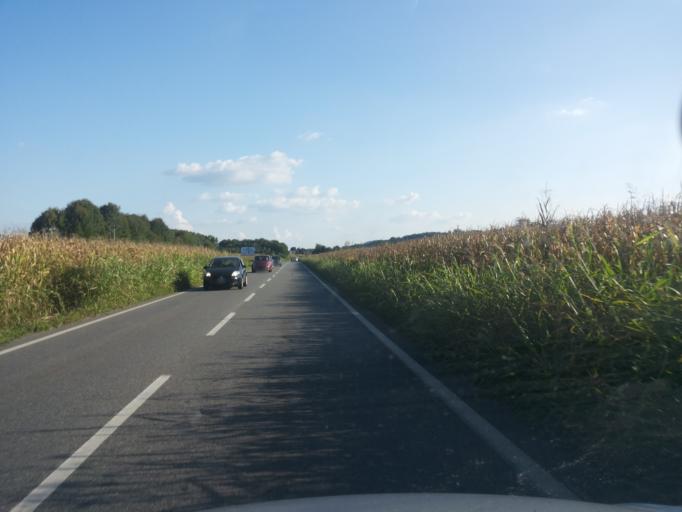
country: IT
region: Piedmont
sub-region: Provincia di Torino
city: Romano Canavese
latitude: 45.4063
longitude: 7.8826
